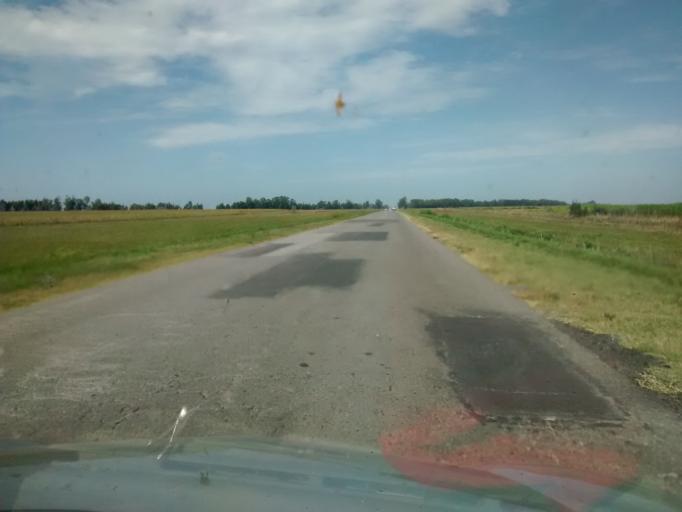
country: AR
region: Buenos Aires
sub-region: Partido de Ayacucho
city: Ayacucho
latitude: -37.1990
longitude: -58.5073
